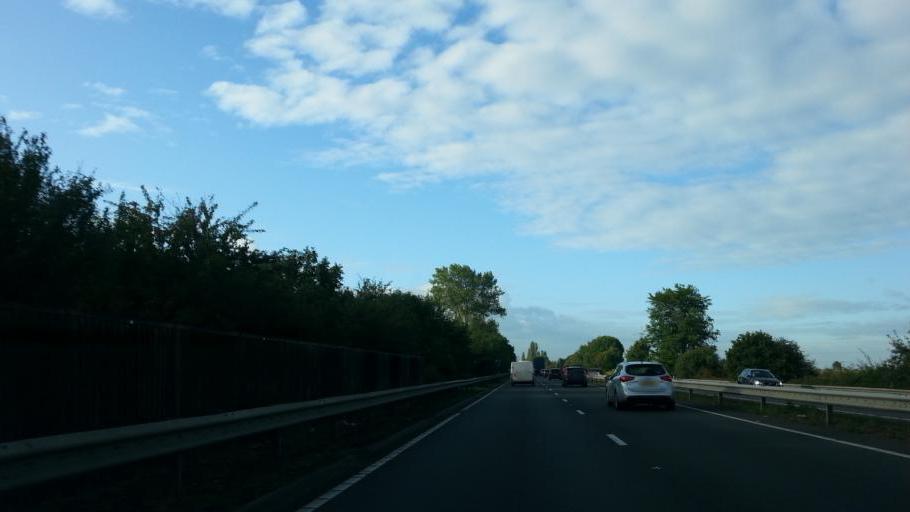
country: GB
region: England
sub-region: Cambridgeshire
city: Eaton Socon
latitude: 52.2260
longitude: -0.2949
